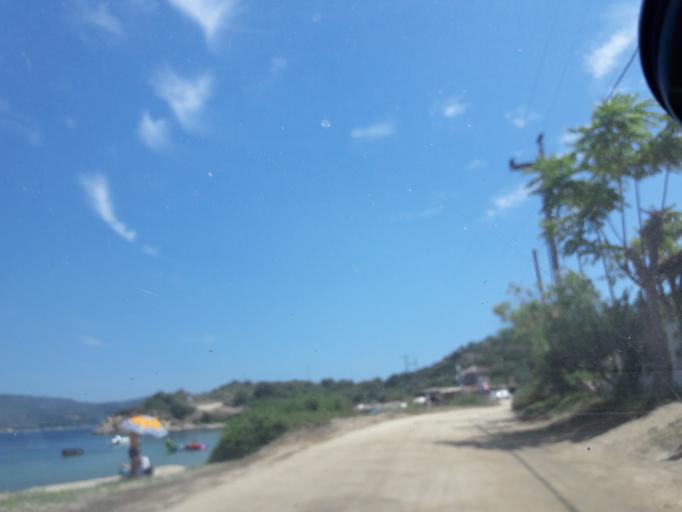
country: GR
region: Central Macedonia
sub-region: Nomos Chalkidikis
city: Ouranoupolis
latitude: 40.3152
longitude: 23.9395
